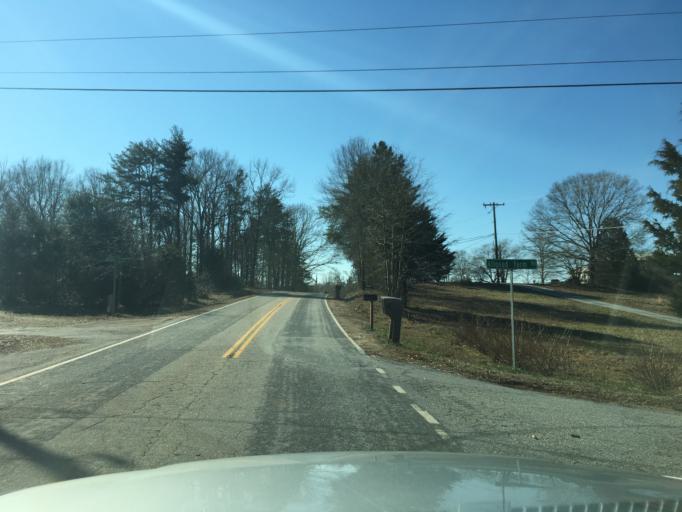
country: US
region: South Carolina
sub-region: Pickens County
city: Pickens
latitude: 34.8680
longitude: -82.7358
